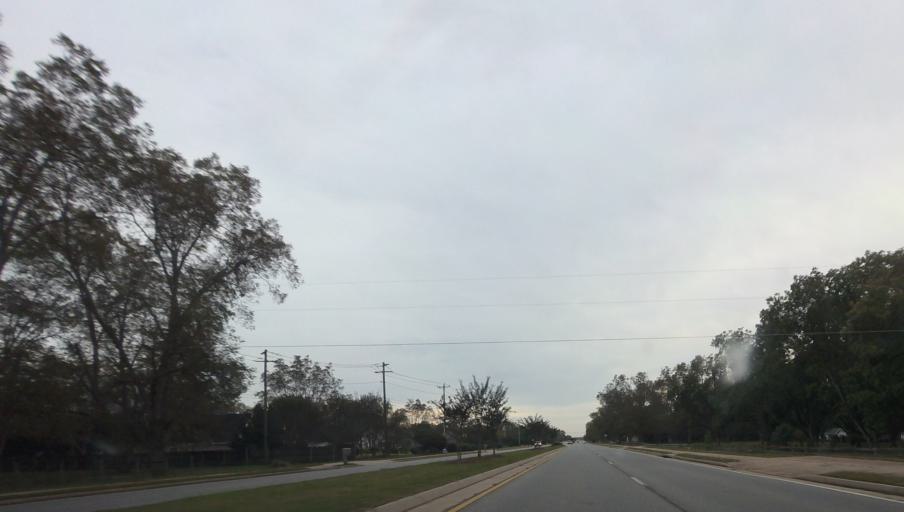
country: US
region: Georgia
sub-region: Houston County
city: Perry
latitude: 32.5229
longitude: -83.6624
